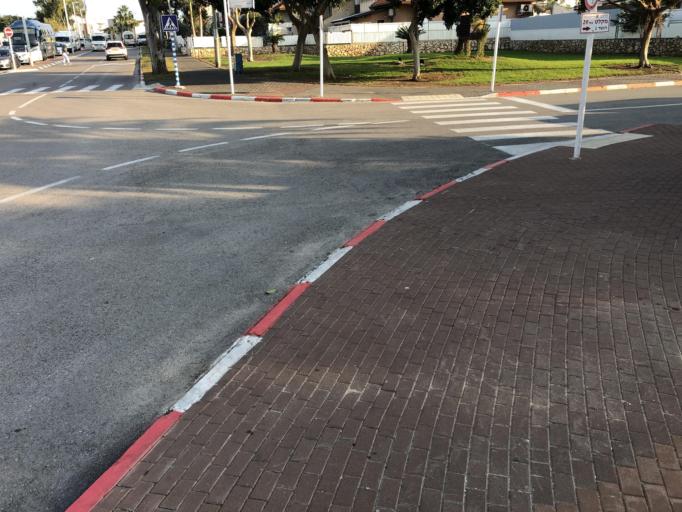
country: IL
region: Northern District
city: `Akko
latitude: 32.9266
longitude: 35.0885
